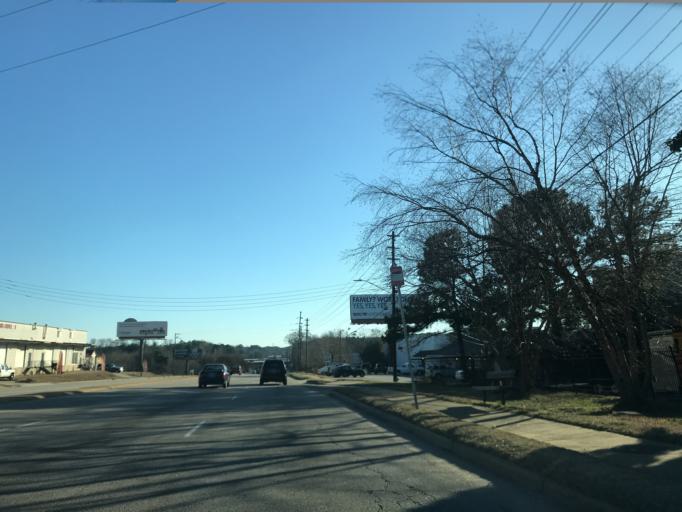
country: US
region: North Carolina
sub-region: Wake County
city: Raleigh
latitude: 35.7578
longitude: -78.6492
